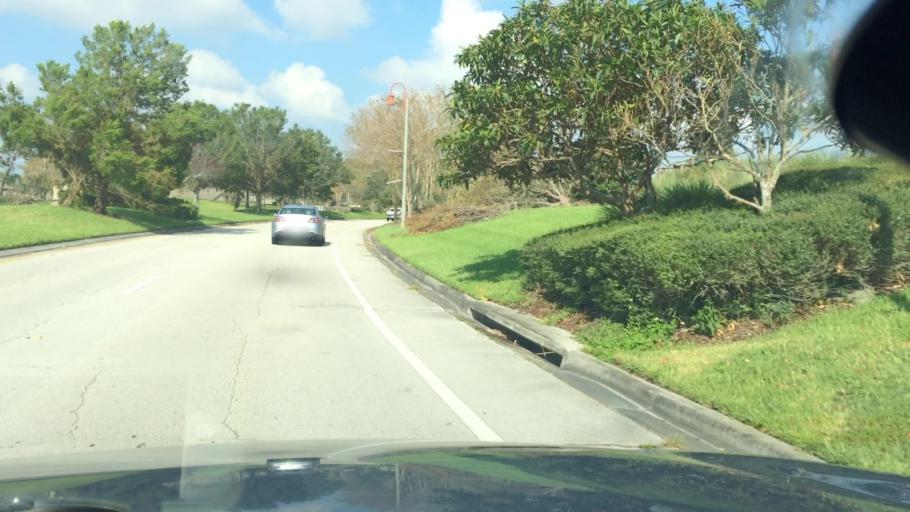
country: US
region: Florida
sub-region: Osceola County
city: Saint Cloud
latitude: 28.2242
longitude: -81.2959
